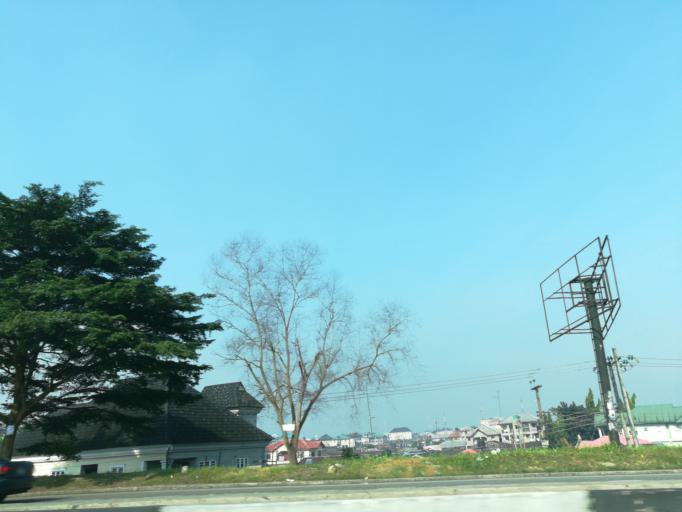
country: NG
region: Rivers
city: Port Harcourt
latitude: 4.8106
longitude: 7.0101
